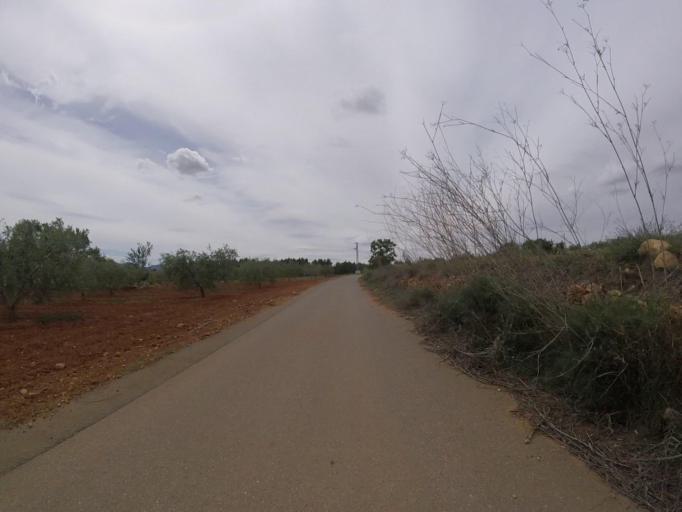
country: ES
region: Valencia
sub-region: Provincia de Castello
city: Benlloch
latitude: 40.1724
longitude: -0.0049
